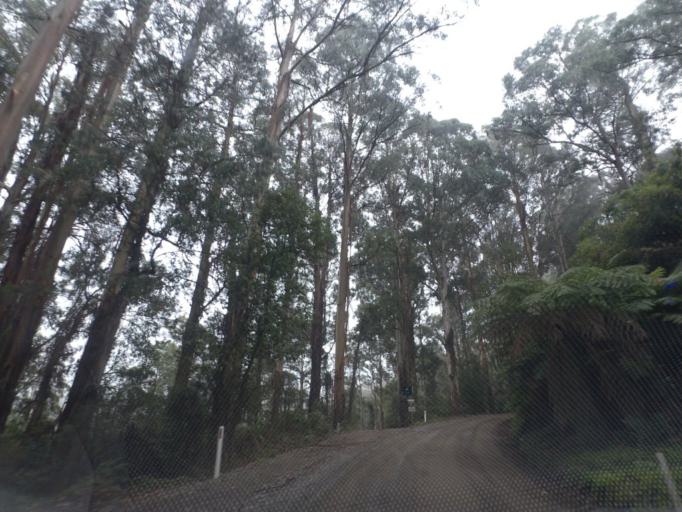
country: AU
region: Victoria
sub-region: Yarra Ranges
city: Launching Place
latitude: -37.7160
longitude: 145.5925
